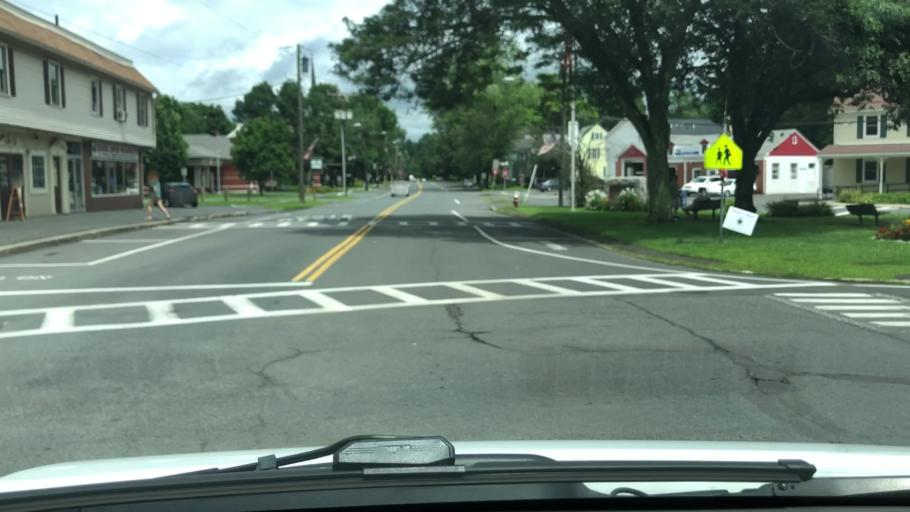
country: US
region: Massachusetts
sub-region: Franklin County
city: South Deerfield
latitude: 42.4773
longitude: -72.6083
